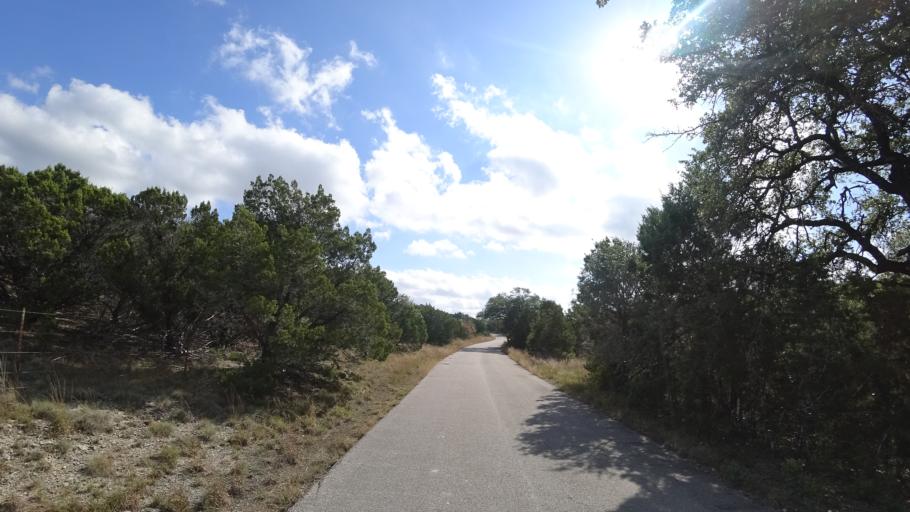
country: US
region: Texas
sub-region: Travis County
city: Bee Cave
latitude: 30.2581
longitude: -97.9418
